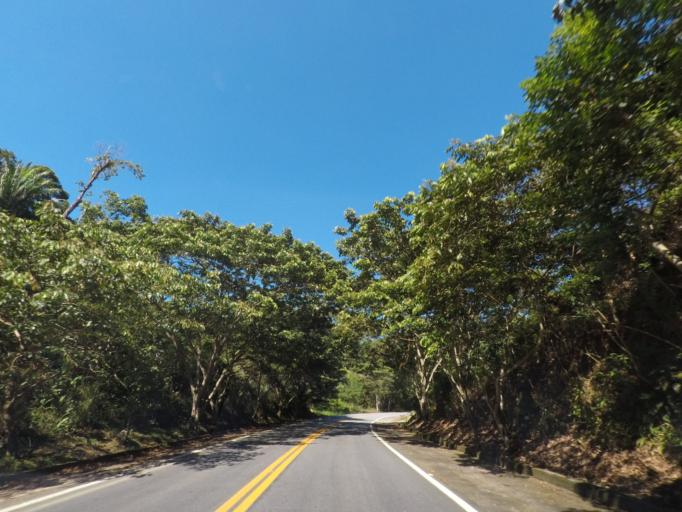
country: BR
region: Rio de Janeiro
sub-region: Parati
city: Paraty
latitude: -23.3423
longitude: -44.7386
